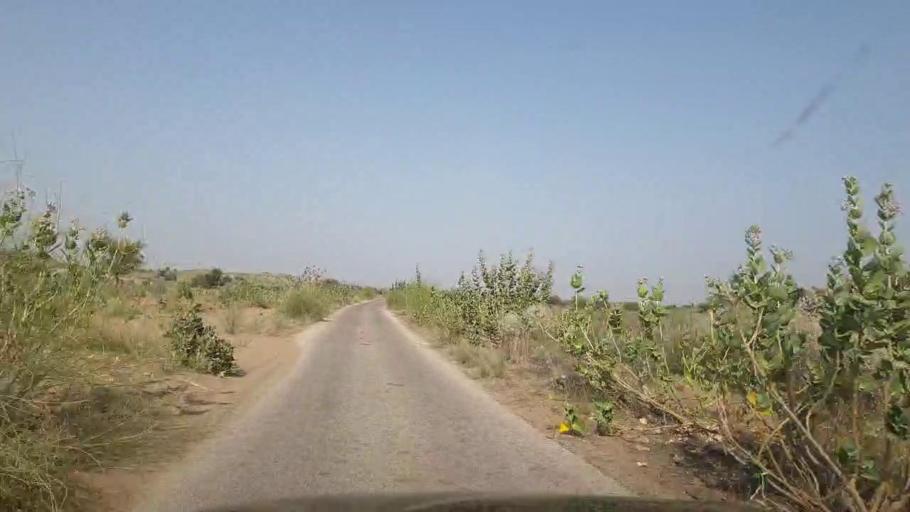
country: PK
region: Sindh
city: Islamkot
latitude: 25.1250
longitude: 70.4476
